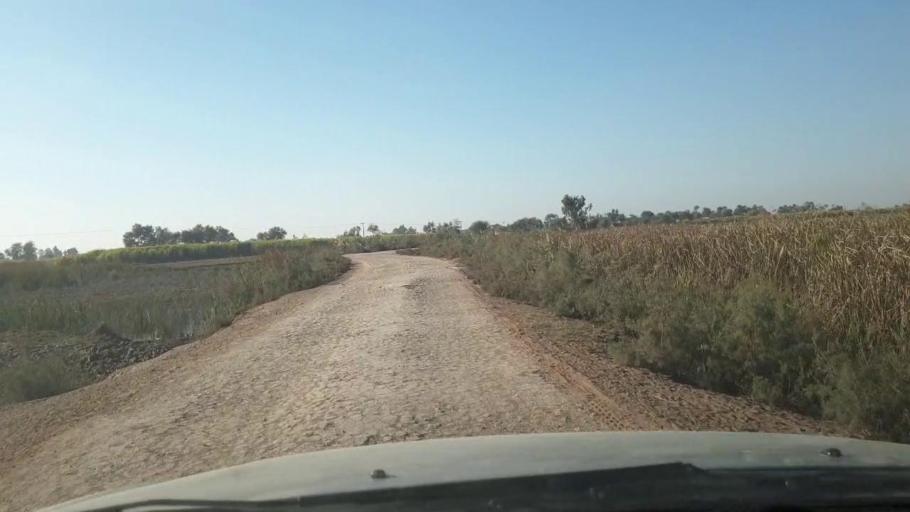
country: PK
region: Sindh
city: Ghotki
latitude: 28.0421
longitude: 69.2964
